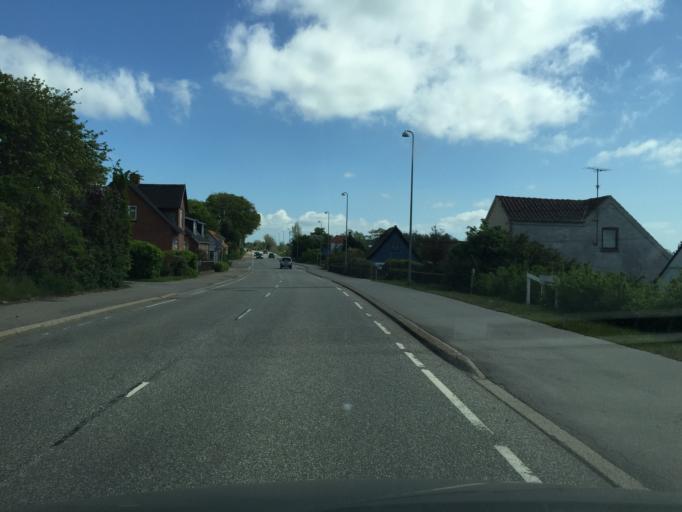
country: DK
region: Zealand
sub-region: Guldborgsund Kommune
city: Stubbekobing
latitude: 54.9961
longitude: 12.1356
